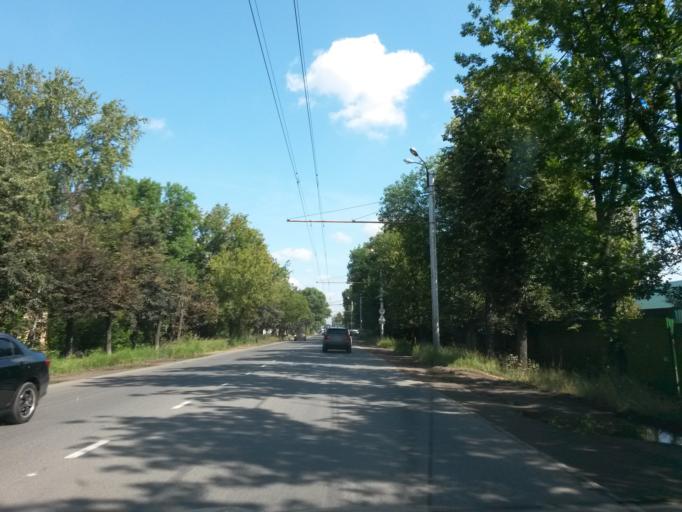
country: RU
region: Ivanovo
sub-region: Gorod Ivanovo
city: Ivanovo
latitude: 57.0047
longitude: 40.9470
